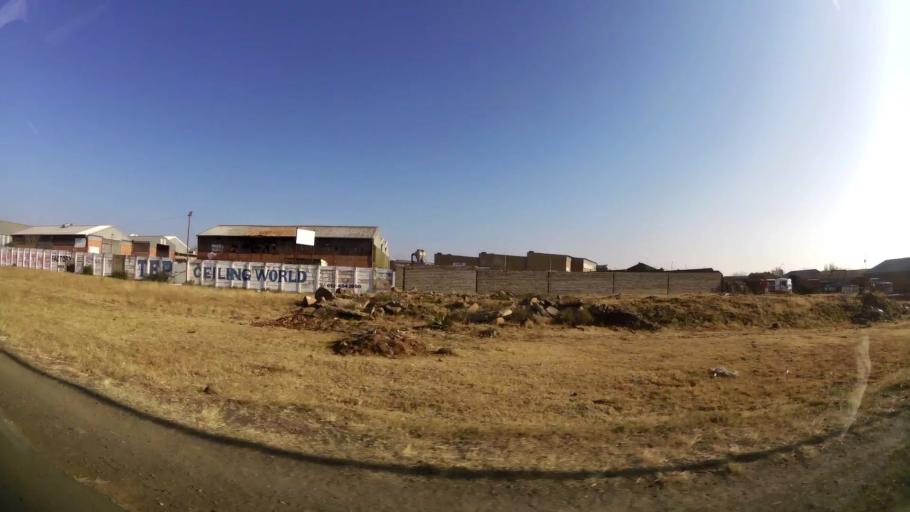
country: ZA
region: Orange Free State
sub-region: Mangaung Metropolitan Municipality
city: Bloemfontein
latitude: -29.1704
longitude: 26.2304
